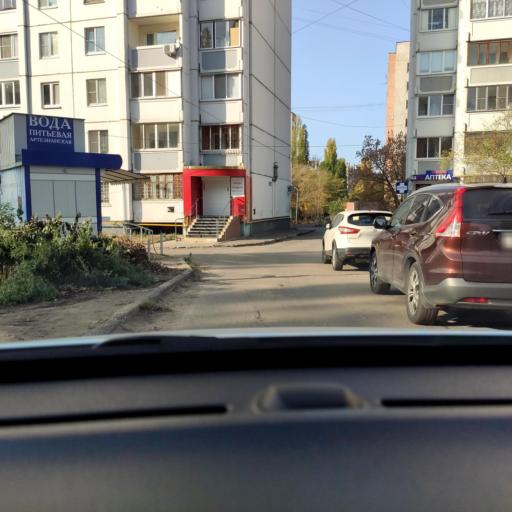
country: RU
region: Voronezj
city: Voronezh
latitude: 51.6925
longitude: 39.2612
